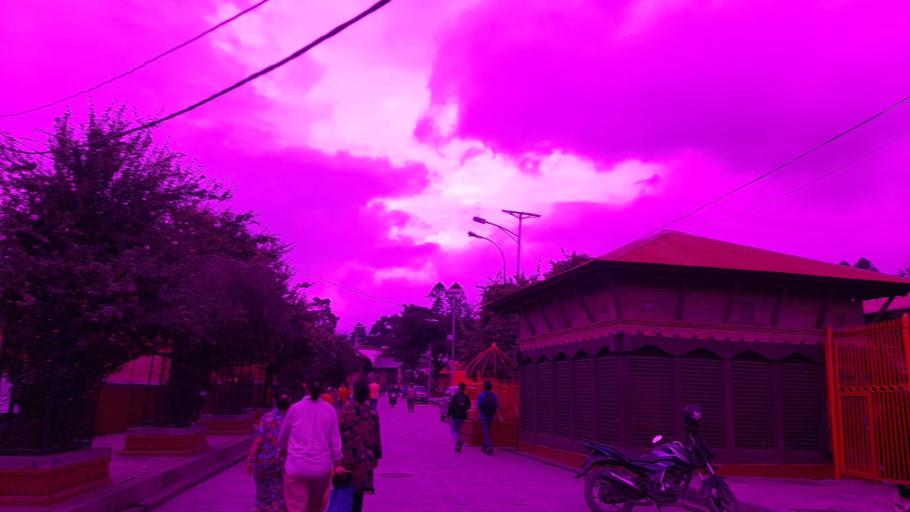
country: NP
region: Central Region
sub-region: Bagmati Zone
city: Kathmandu
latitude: 27.7083
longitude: 85.3477
